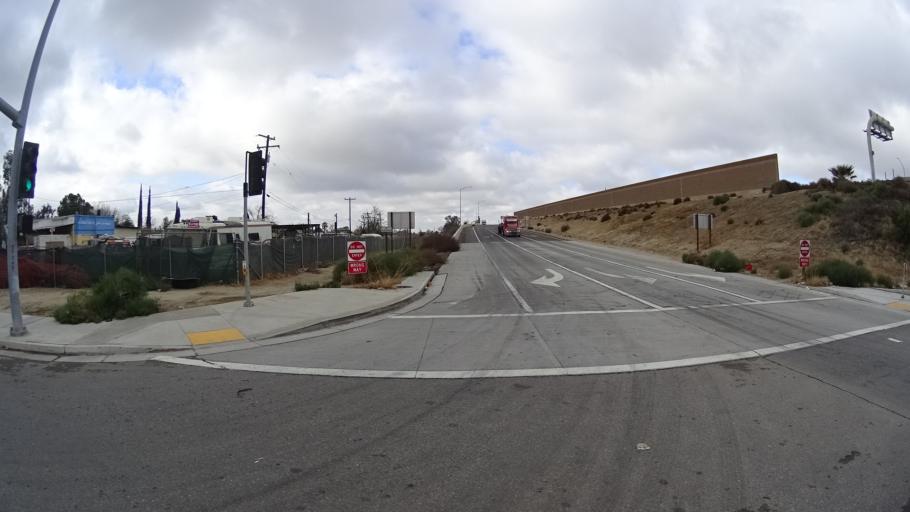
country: US
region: California
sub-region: Kern County
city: Bakersfield
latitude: 35.3518
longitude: -118.9854
